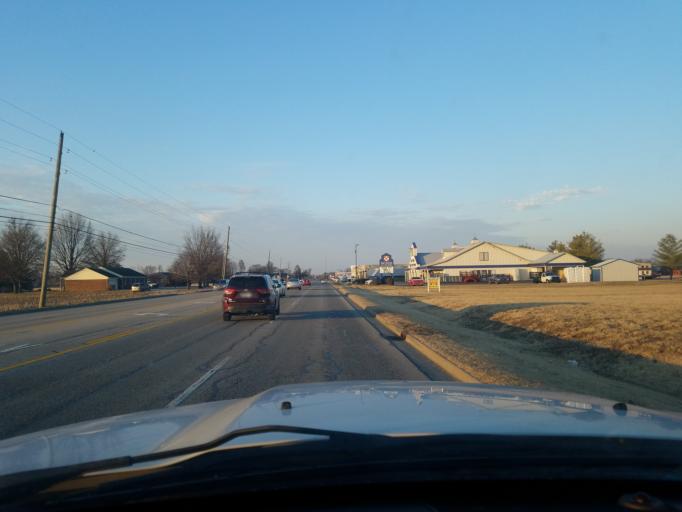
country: US
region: Indiana
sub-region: Vanderburgh County
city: Melody Hill
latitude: 38.0070
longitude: -87.4738
